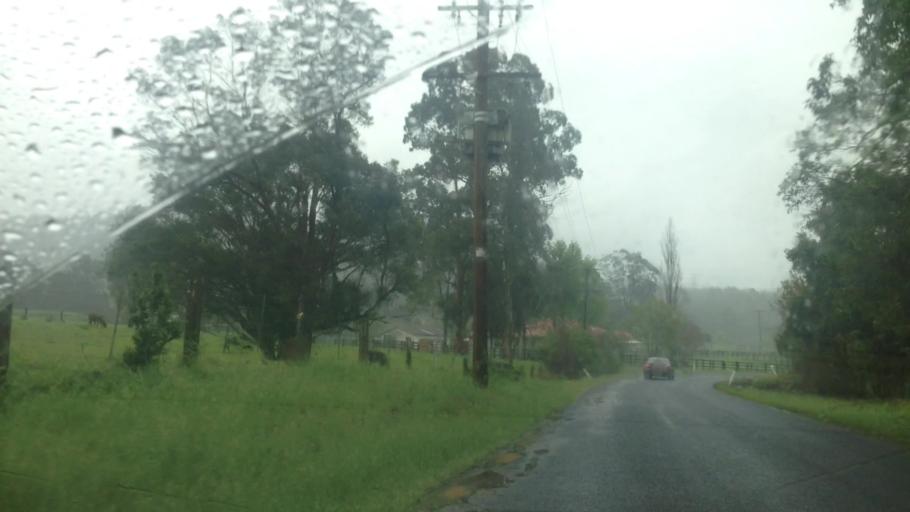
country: AU
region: New South Wales
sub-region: Wyong Shire
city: Little Jilliby
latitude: -33.2069
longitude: 151.3645
